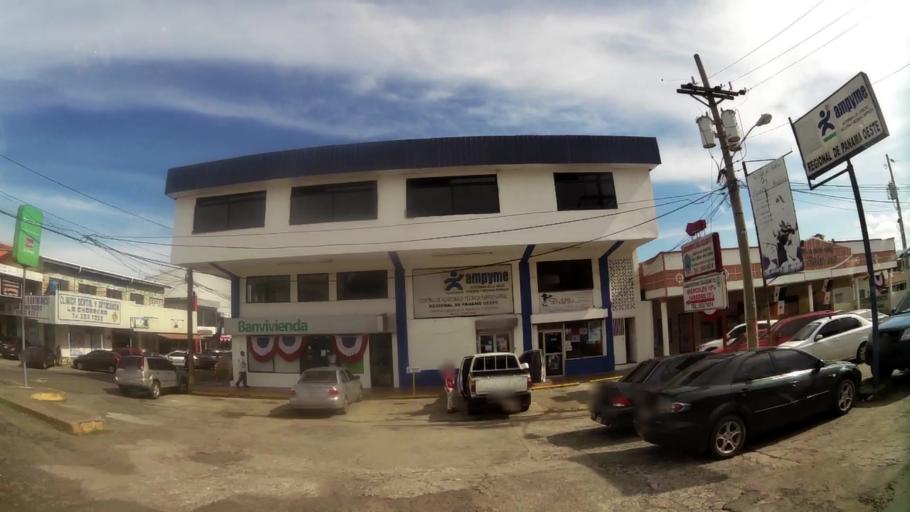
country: PA
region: Panama
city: La Chorrera
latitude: 8.8849
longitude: -79.7758
